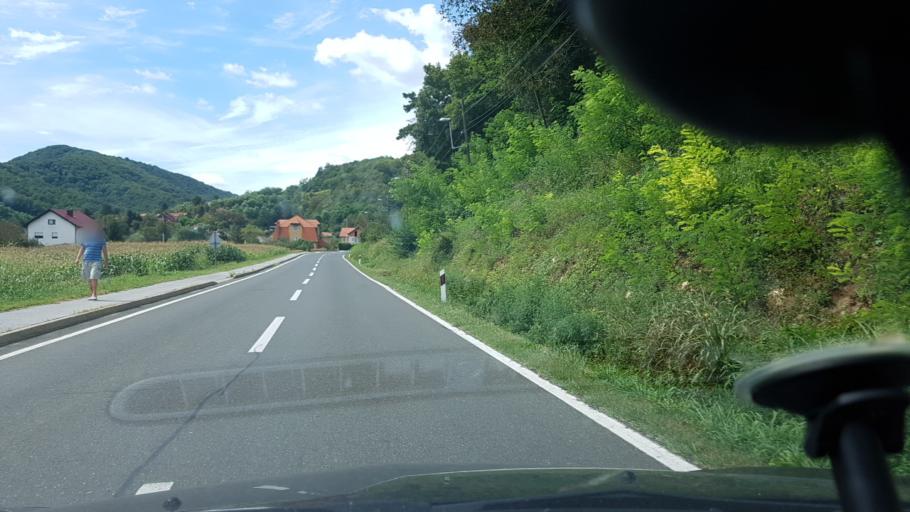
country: HR
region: Varazdinska
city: Lepoglava
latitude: 46.2075
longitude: 16.0252
